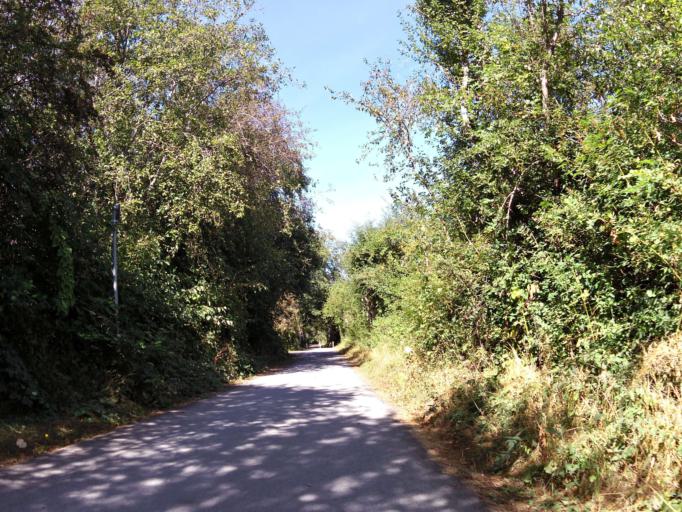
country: CA
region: British Columbia
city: Victoria
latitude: 48.5406
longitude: -123.3816
